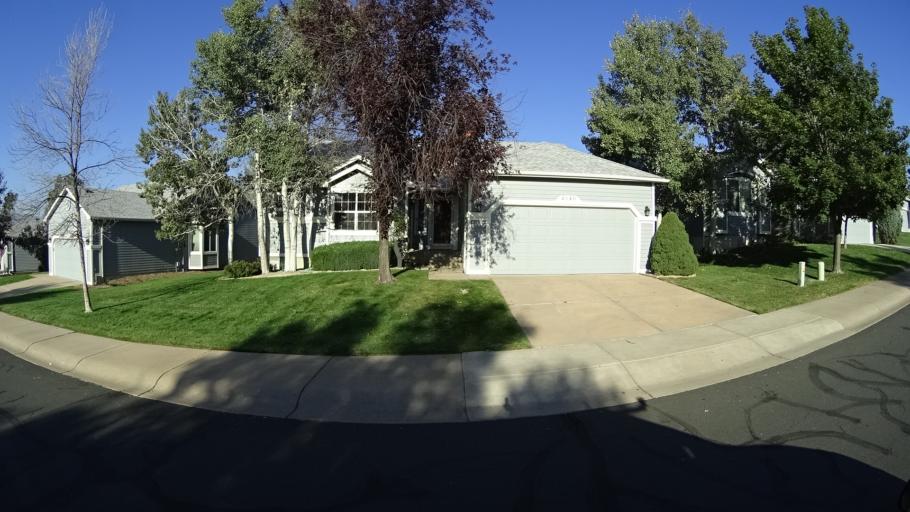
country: US
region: Colorado
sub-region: El Paso County
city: Cimarron Hills
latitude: 38.8900
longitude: -104.7060
